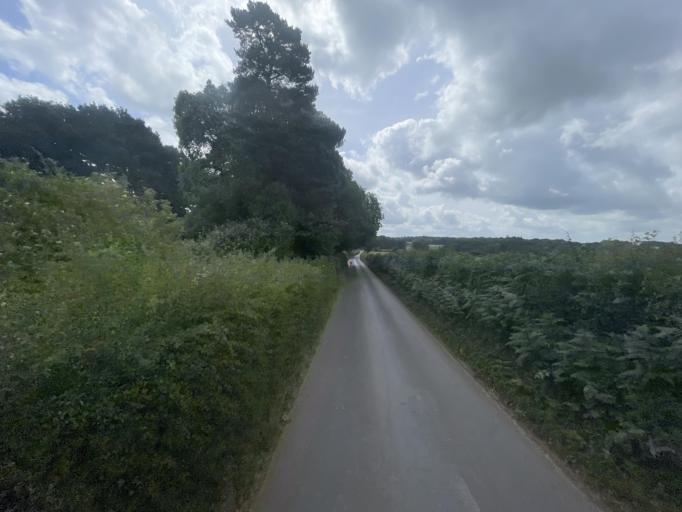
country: GB
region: England
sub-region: Kent
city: Edenbridge
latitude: 51.1601
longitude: 0.1462
